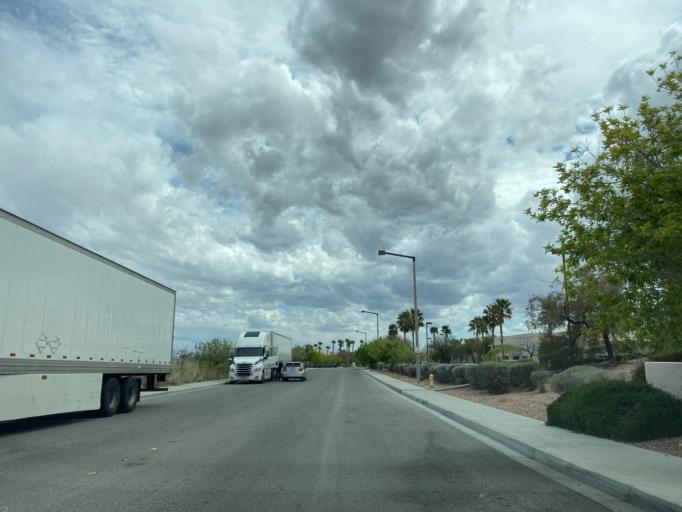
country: US
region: Nevada
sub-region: Clark County
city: Summerlin South
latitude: 36.1892
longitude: -115.3135
